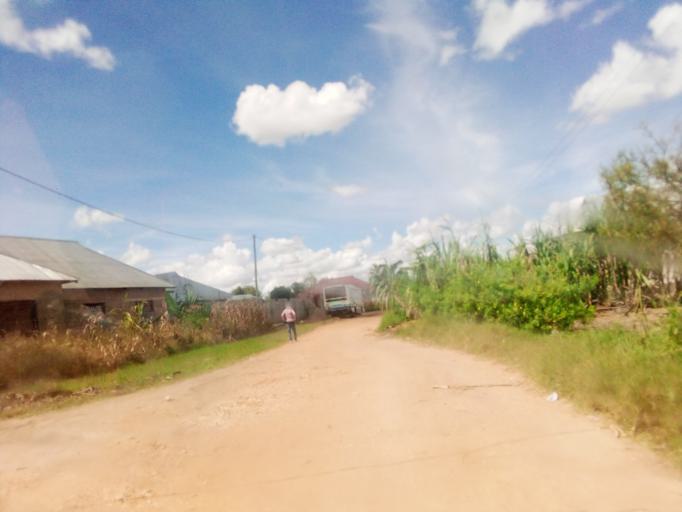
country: TZ
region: Dodoma
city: Dodoma
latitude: -6.1630
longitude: 35.7642
